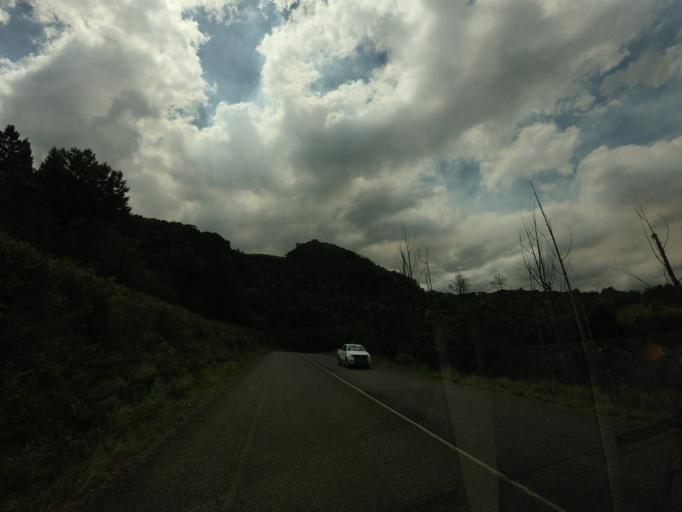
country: ZA
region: Mpumalanga
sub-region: Ehlanzeni District
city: Graksop
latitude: -24.9452
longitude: 30.8106
